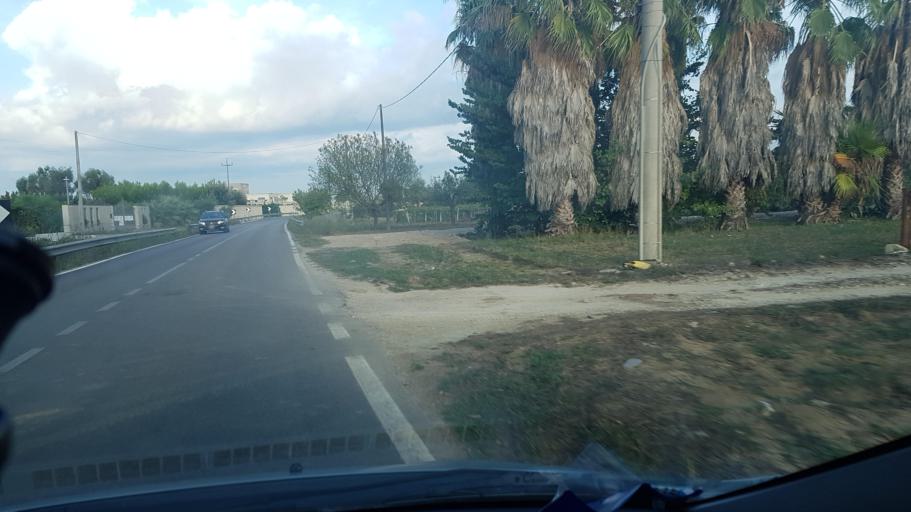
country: IT
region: Apulia
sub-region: Provincia di Lecce
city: Carmiano
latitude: 40.3449
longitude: 18.0195
